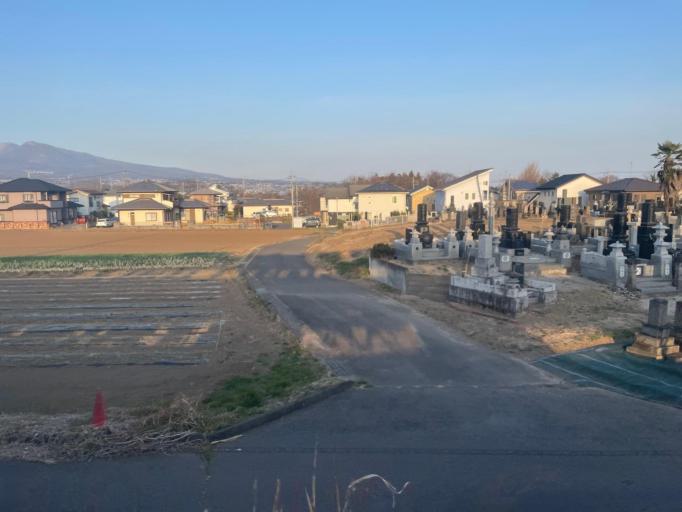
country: JP
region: Gunma
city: Kanekomachi
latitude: 36.4342
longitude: 139.0285
